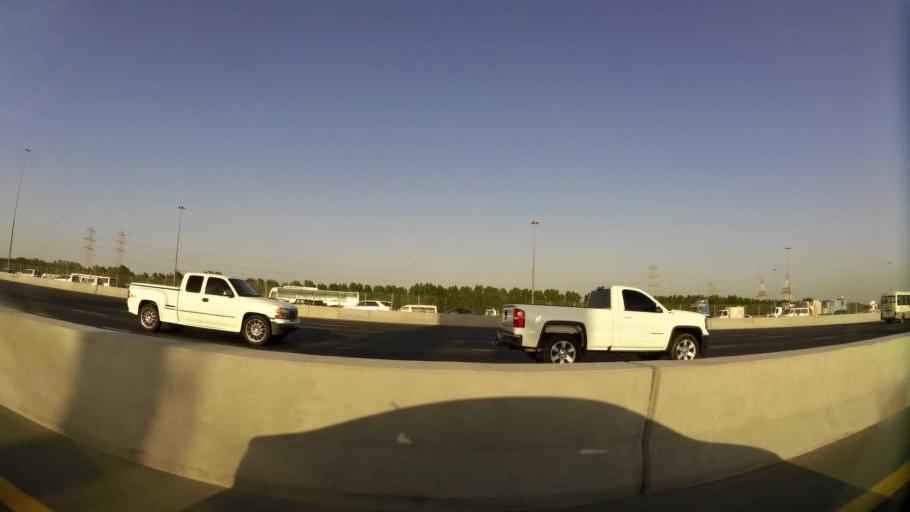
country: AE
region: Ash Shariqah
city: Sharjah
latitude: 25.2387
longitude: 55.4036
